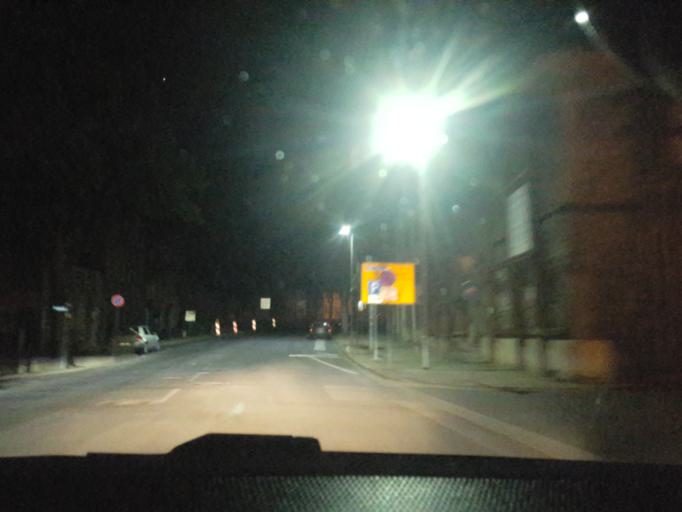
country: DE
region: Saxony-Anhalt
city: Wimmelburg
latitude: 51.5280
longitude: 11.5395
